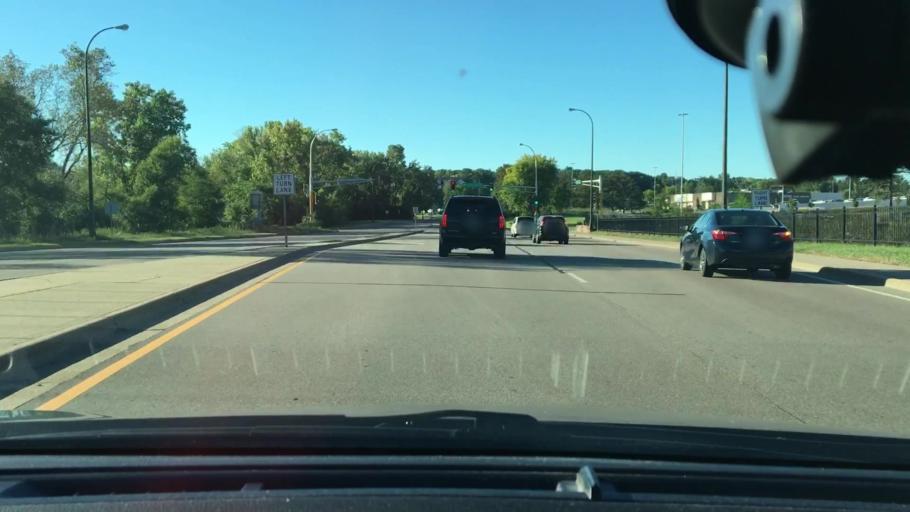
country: US
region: Minnesota
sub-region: Hennepin County
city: Minnetonka Mills
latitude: 44.9702
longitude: -93.4330
